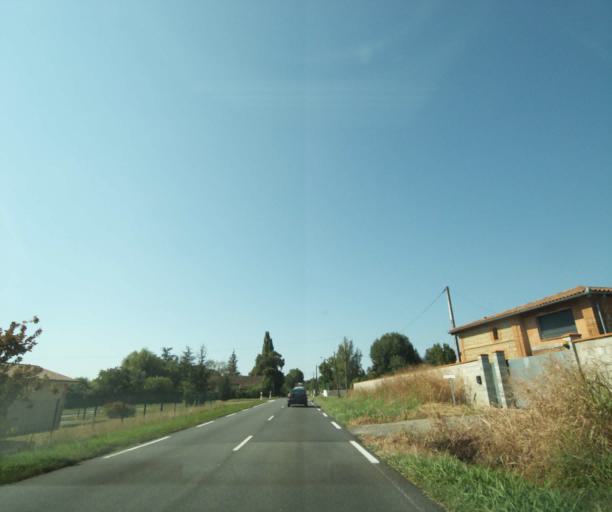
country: FR
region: Midi-Pyrenees
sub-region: Departement de la Haute-Garonne
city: Saint-Sulpice-sur-Leze
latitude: 43.3421
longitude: 1.3228
